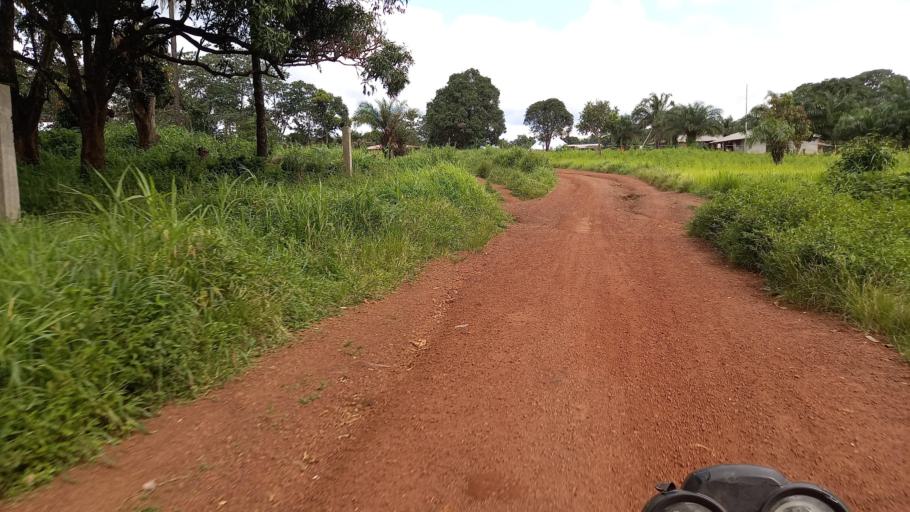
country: SL
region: Northern Province
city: Kamakwie
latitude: 9.5033
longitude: -12.2387
